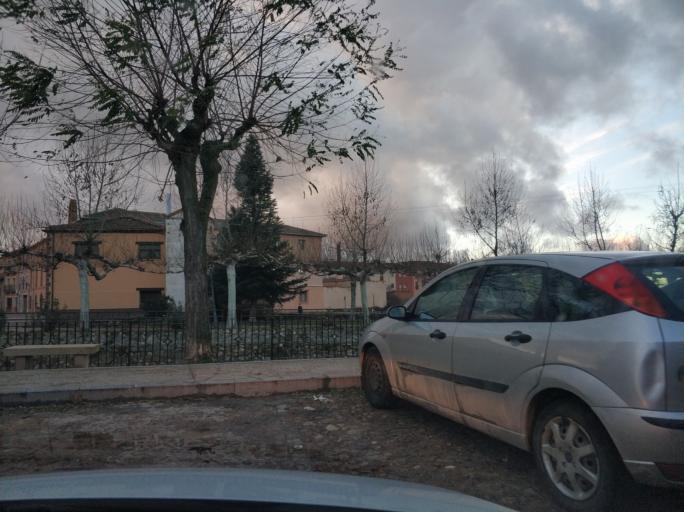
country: ES
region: Castille and Leon
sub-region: Provincia de Segovia
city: Ayllon
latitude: 41.4195
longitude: -3.3776
